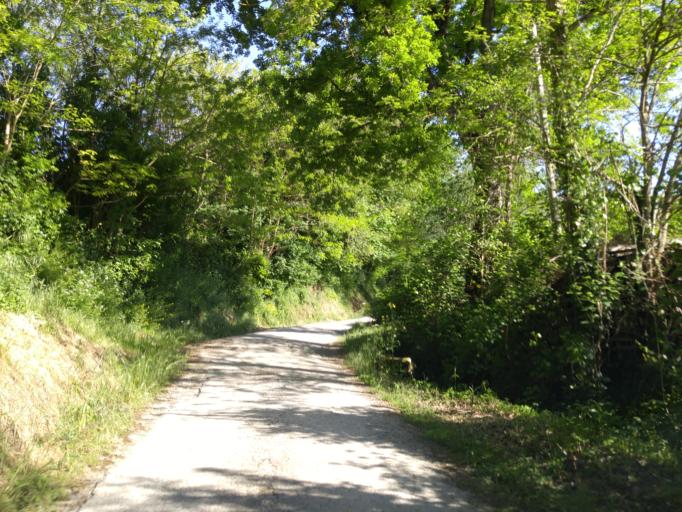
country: IT
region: The Marches
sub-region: Provincia di Pesaro e Urbino
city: Mombaroccio
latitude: 43.8104
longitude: 12.8421
